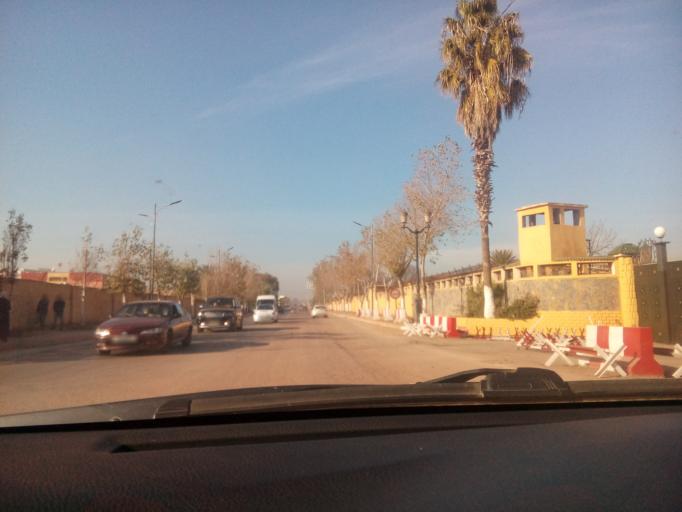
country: DZ
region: Oran
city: Es Senia
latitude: 35.6537
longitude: -0.6147
